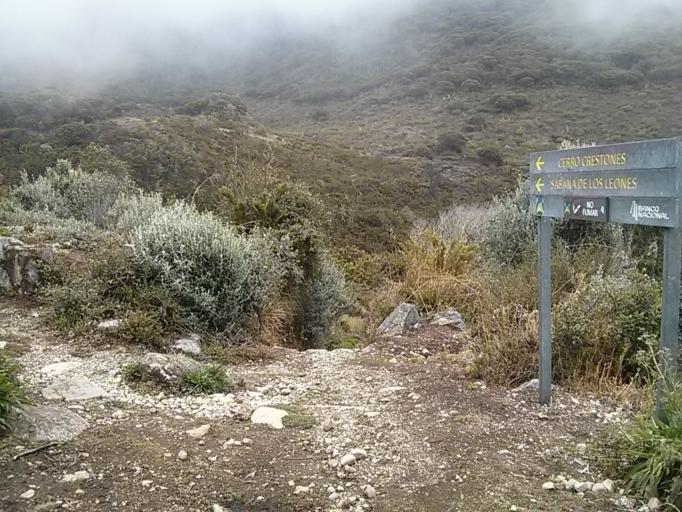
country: CR
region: San Jose
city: Daniel Flores
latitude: 9.4567
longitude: -83.5050
